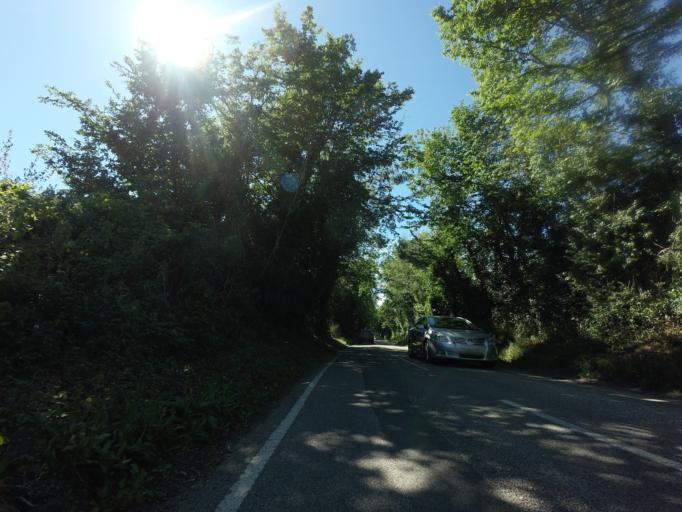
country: GB
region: England
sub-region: Kent
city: Birchington-on-Sea
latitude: 51.3353
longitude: 1.3278
